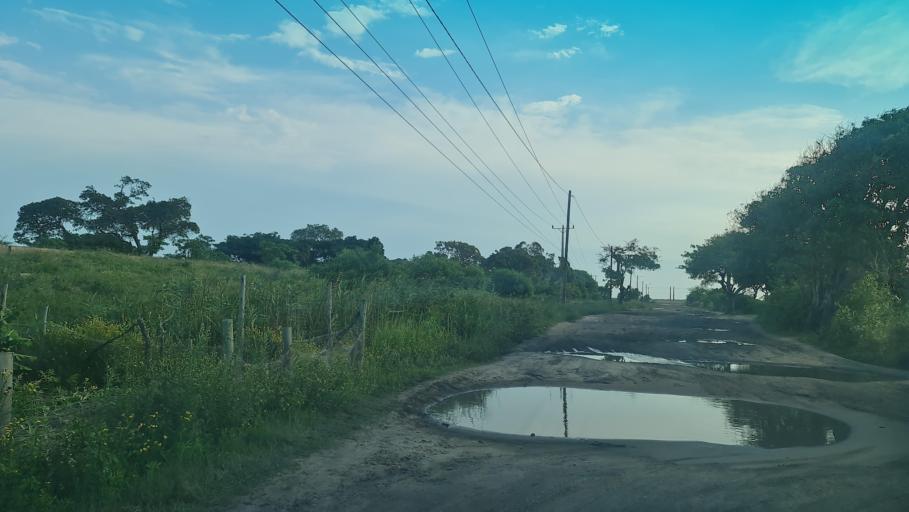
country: MZ
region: Maputo City
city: Maputo
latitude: -25.7365
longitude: 32.7310
